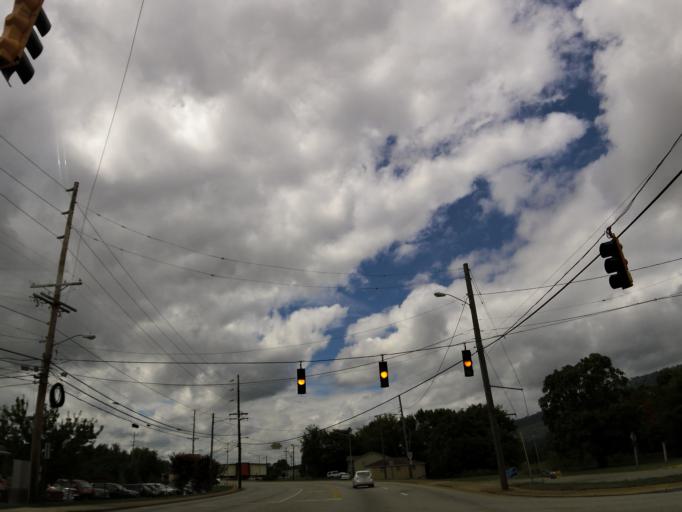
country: US
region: Tennessee
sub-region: Hamilton County
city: Chattanooga
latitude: 35.0258
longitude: -85.3115
